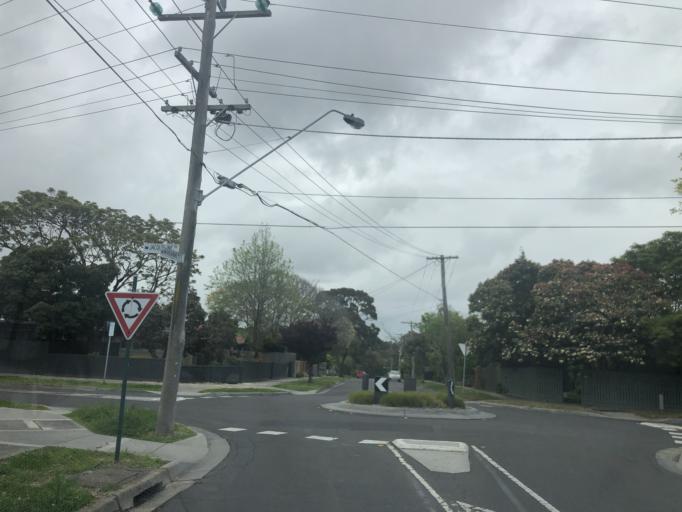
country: AU
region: Victoria
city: Burwood East
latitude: -37.8644
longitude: 145.1354
